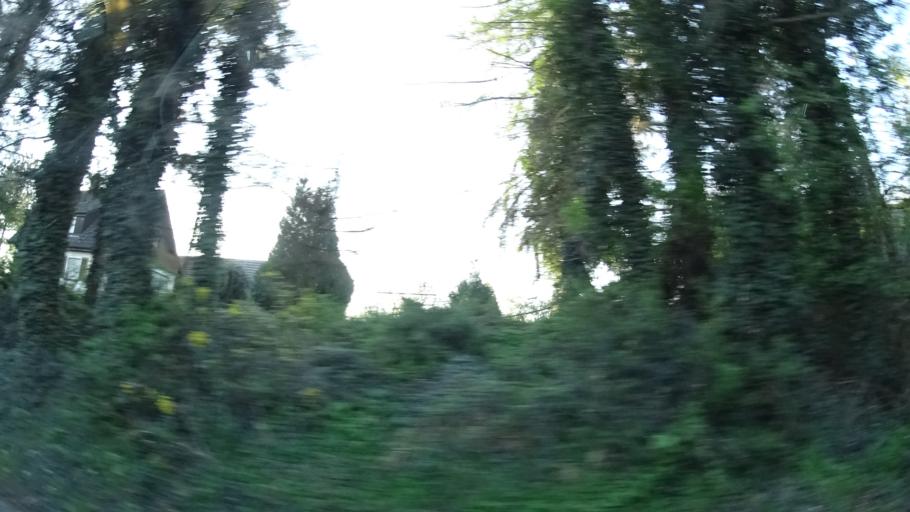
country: DE
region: Baden-Wuerttemberg
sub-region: Regierungsbezirk Stuttgart
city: Pfedelbach
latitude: 49.1711
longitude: 9.5016
